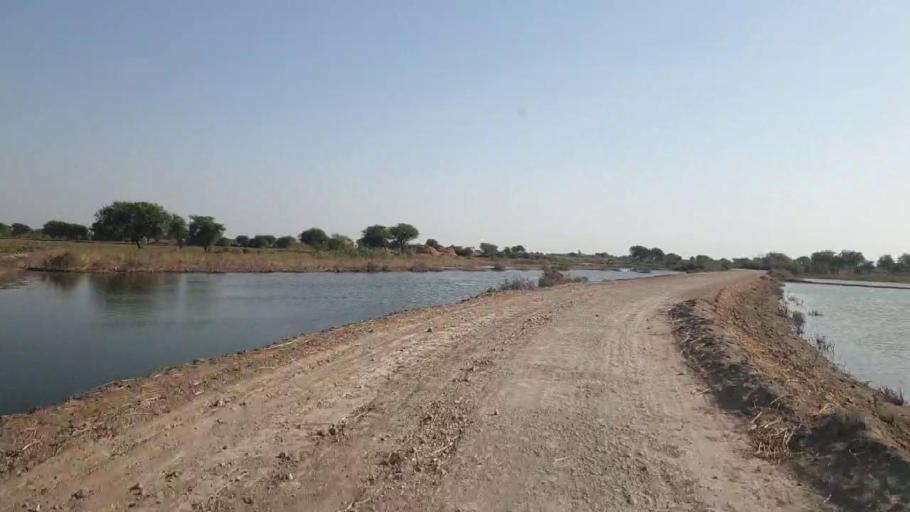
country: PK
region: Sindh
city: Matli
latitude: 25.0064
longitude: 68.7437
